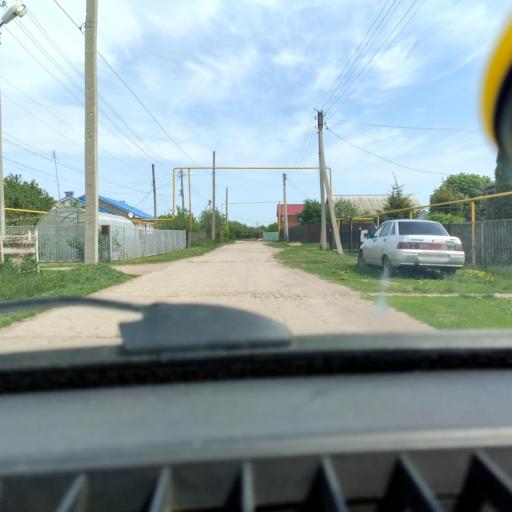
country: RU
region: Samara
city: Povolzhskiy
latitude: 53.6447
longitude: 49.6874
